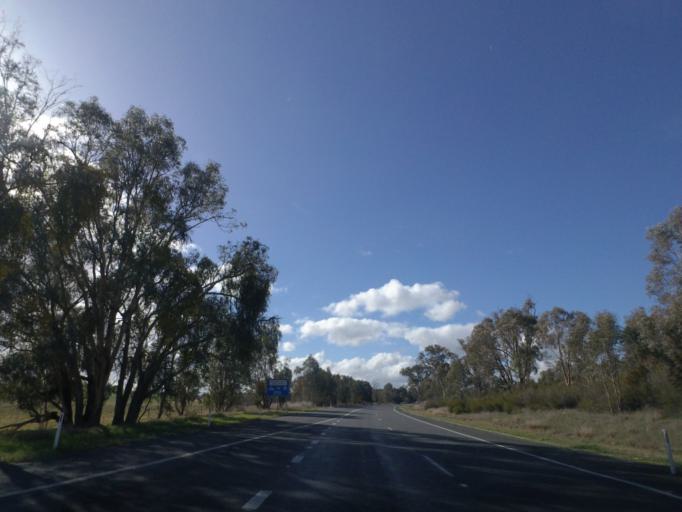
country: AU
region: New South Wales
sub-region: Greater Hume Shire
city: Holbrook
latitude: -35.8960
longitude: 147.1672
